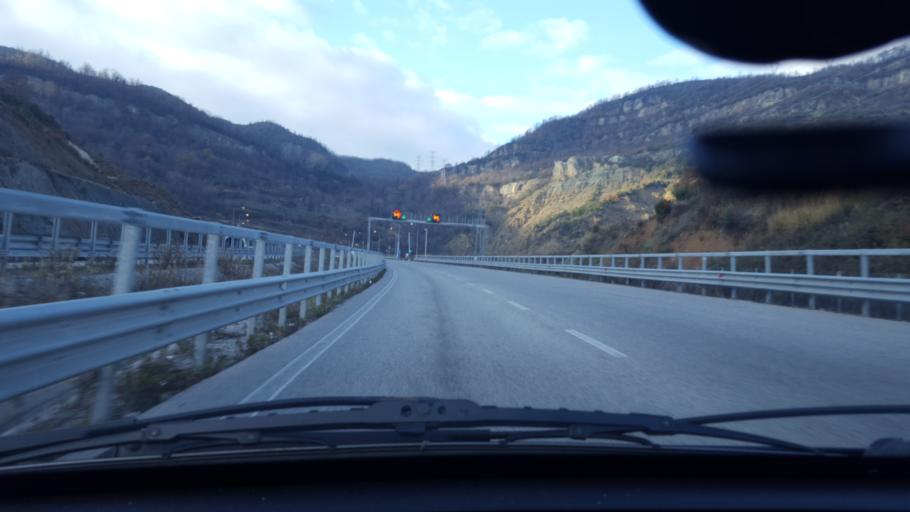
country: AL
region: Tirane
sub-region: Rrethi i Tiranes
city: Krrabe
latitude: 41.1934
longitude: 19.9899
